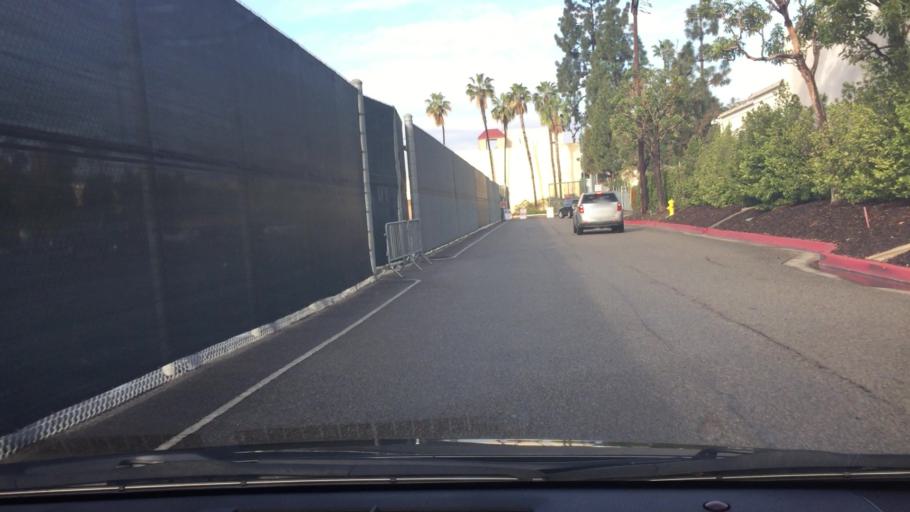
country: US
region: California
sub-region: Orange County
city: Anaheim
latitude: 33.8088
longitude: -117.9120
